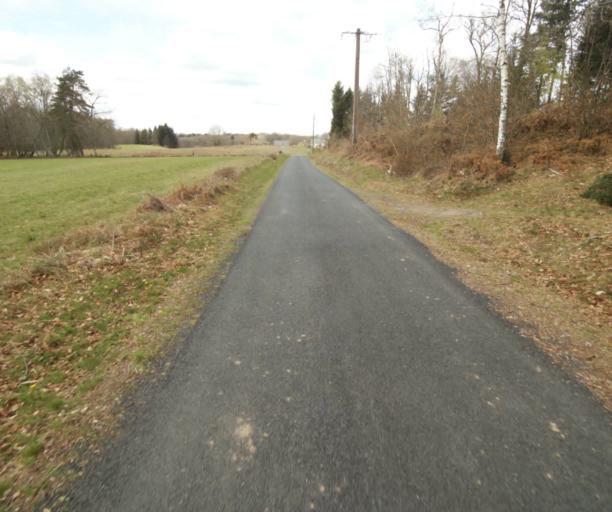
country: FR
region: Limousin
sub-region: Departement de la Correze
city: Argentat
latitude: 45.2169
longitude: 1.9254
